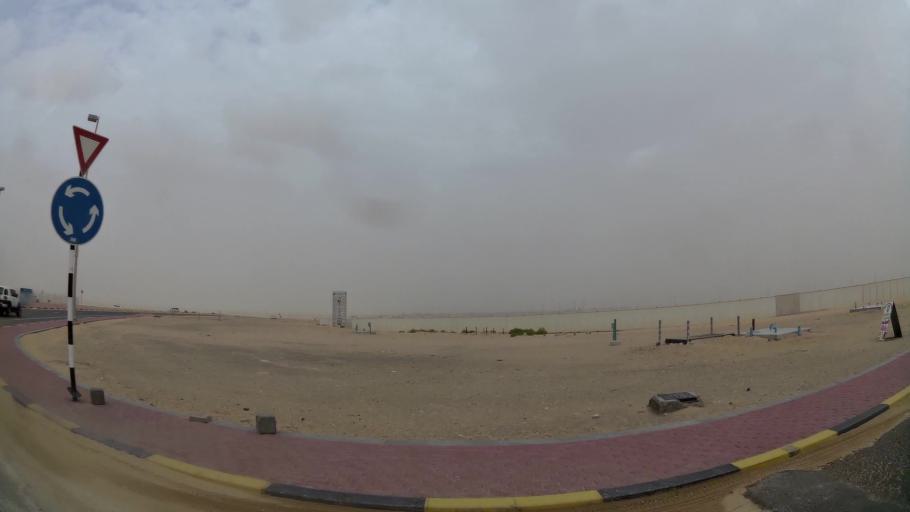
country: AE
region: Abu Dhabi
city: Abu Dhabi
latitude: 24.4259
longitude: 54.7132
